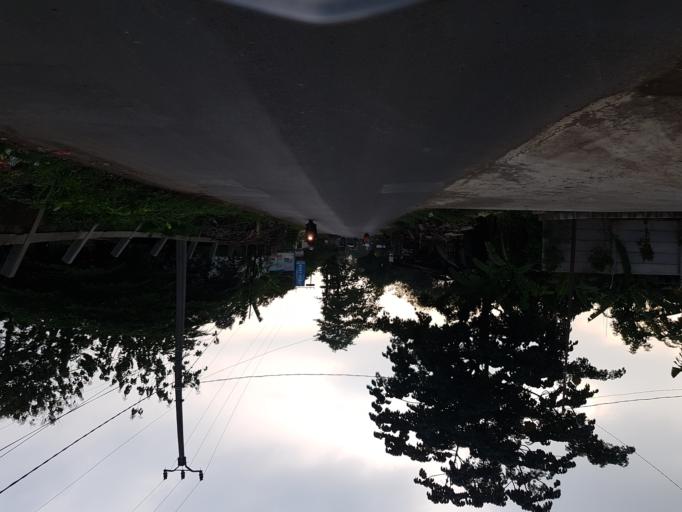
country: ID
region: West Java
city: Parung
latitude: -6.4737
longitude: 106.7217
